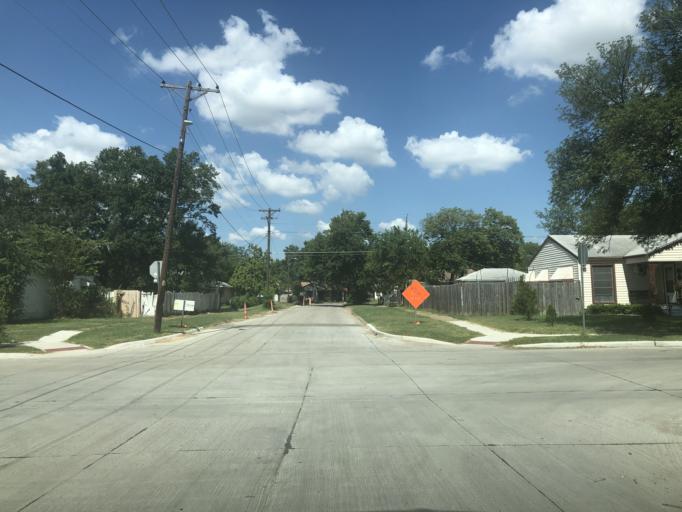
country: US
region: Texas
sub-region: Dallas County
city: Grand Prairie
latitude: 32.7331
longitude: -97.0079
